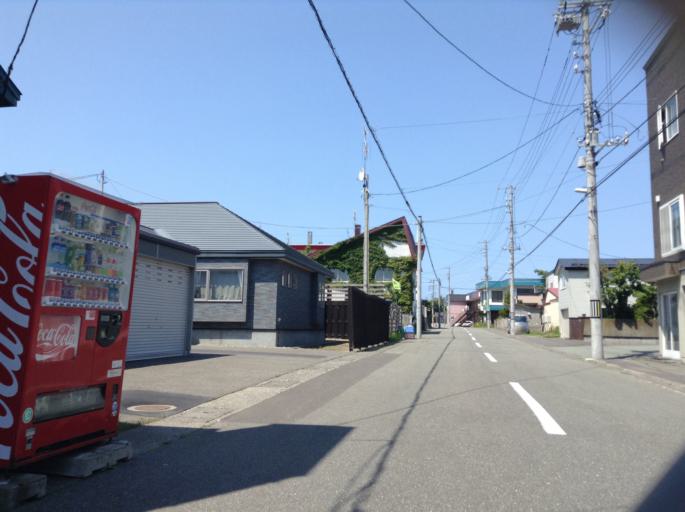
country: JP
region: Hokkaido
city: Wakkanai
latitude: 45.4220
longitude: 141.6717
